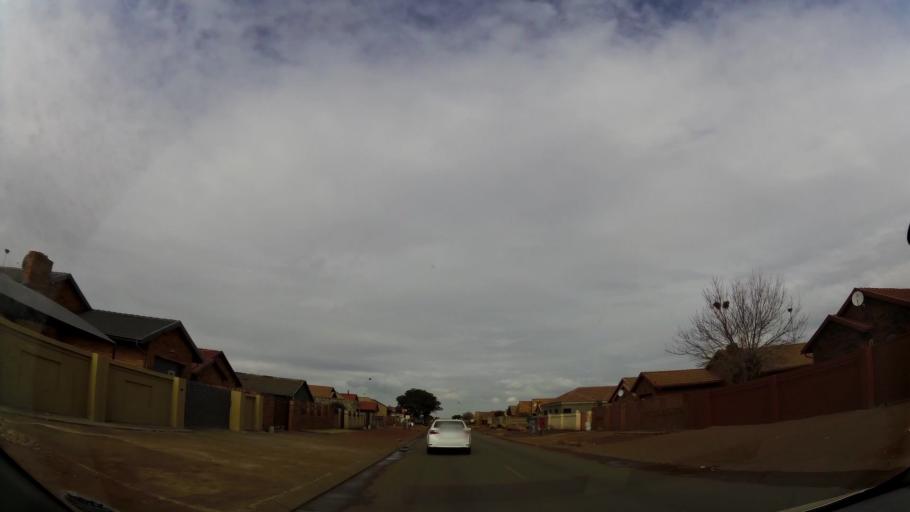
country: ZA
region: Gauteng
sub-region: Ekurhuleni Metropolitan Municipality
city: Germiston
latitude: -26.3722
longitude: 28.1551
